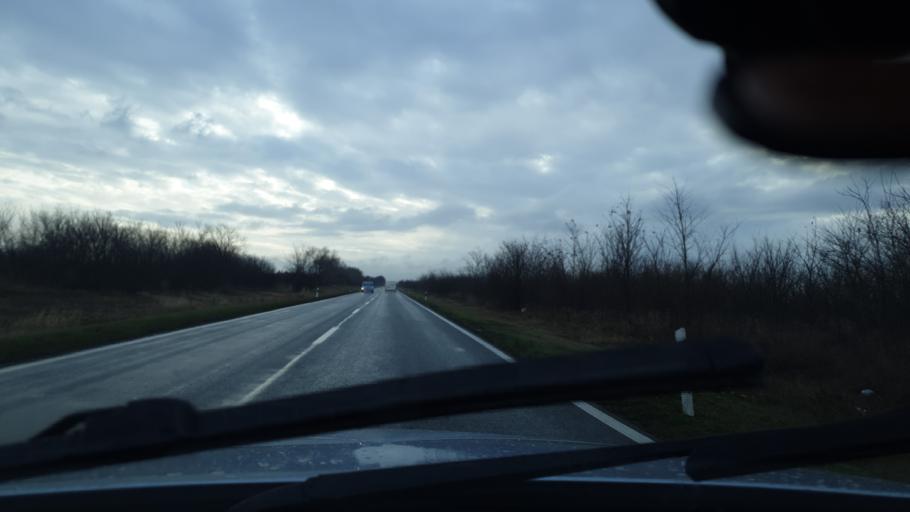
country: RS
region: Autonomna Pokrajina Vojvodina
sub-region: Juznobanatski Okrug
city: Kovin
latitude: 44.7679
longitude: 20.9484
